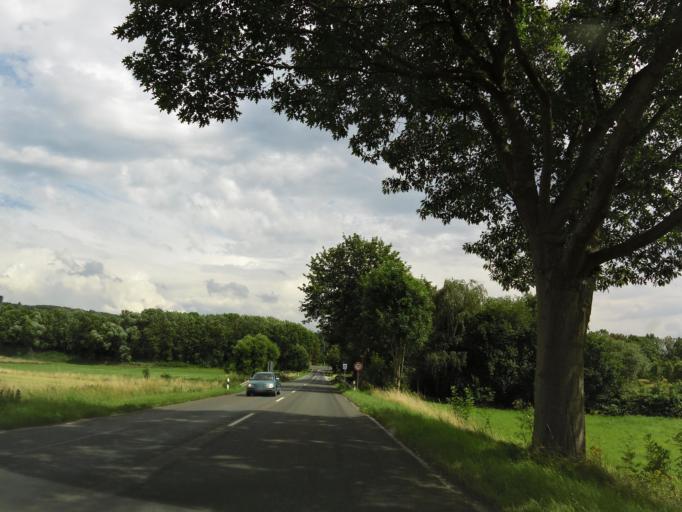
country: DE
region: Lower Saxony
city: Boffzen
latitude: 51.7623
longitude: 9.4032
